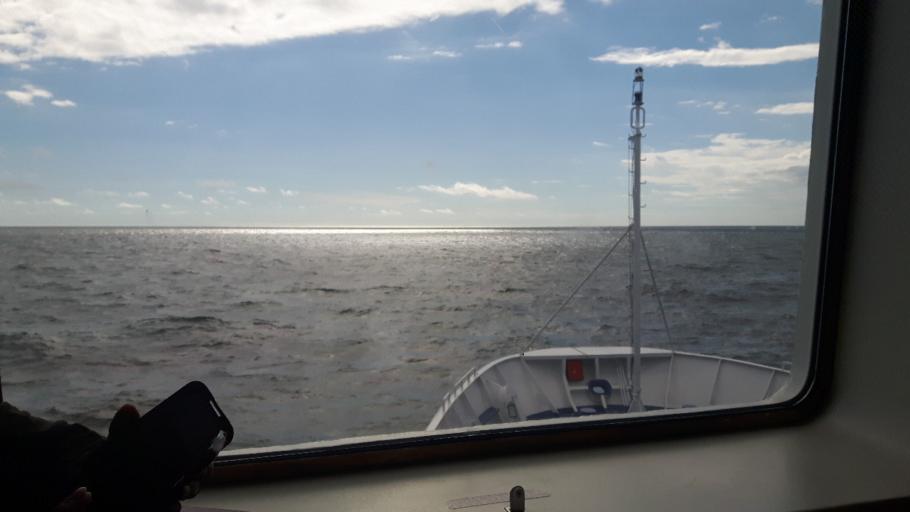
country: LV
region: Liepaja
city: Liepaja
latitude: 56.4315
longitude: 20.4048
